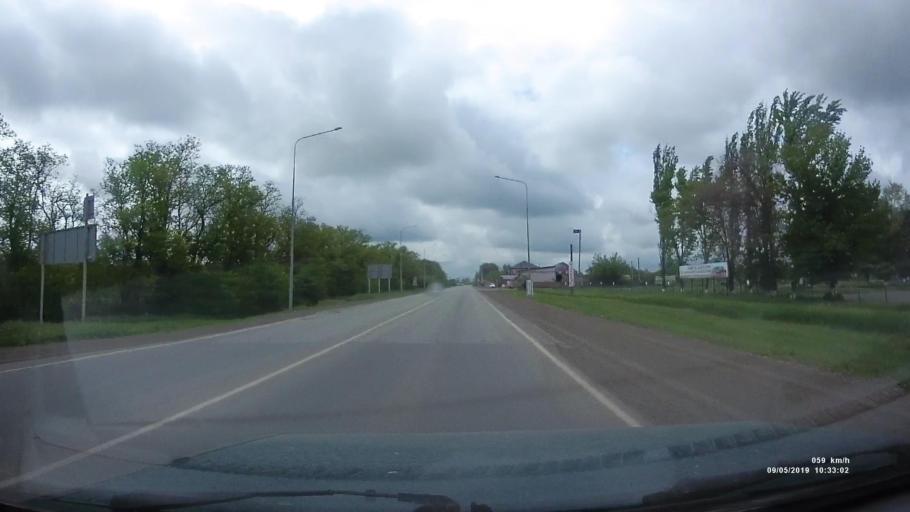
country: RU
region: Rostov
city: Azov
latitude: 47.0669
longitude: 39.4254
